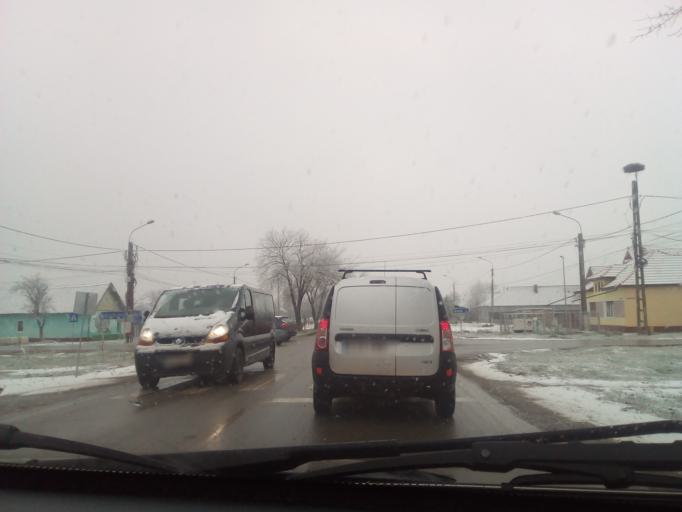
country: RO
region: Timis
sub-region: Comuna Mosnita Noua
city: Mosnita Noua
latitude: 45.7184
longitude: 21.3259
